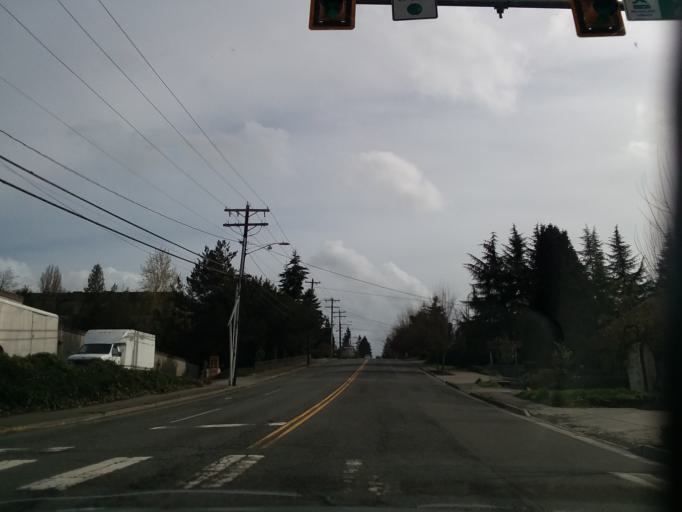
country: US
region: Washington
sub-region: Snohomish County
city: Lynnwood
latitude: 47.8030
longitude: -122.3219
